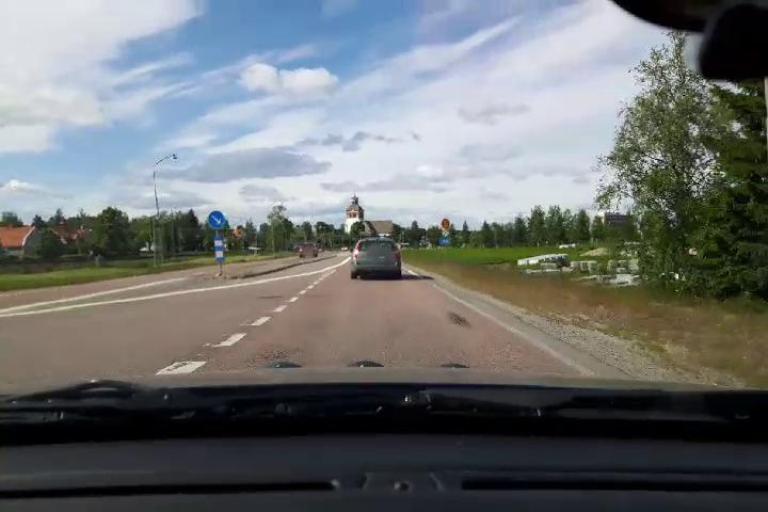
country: SE
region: Gaevleborg
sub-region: Bollnas Kommun
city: Bollnas
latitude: 61.3414
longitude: 16.3928
